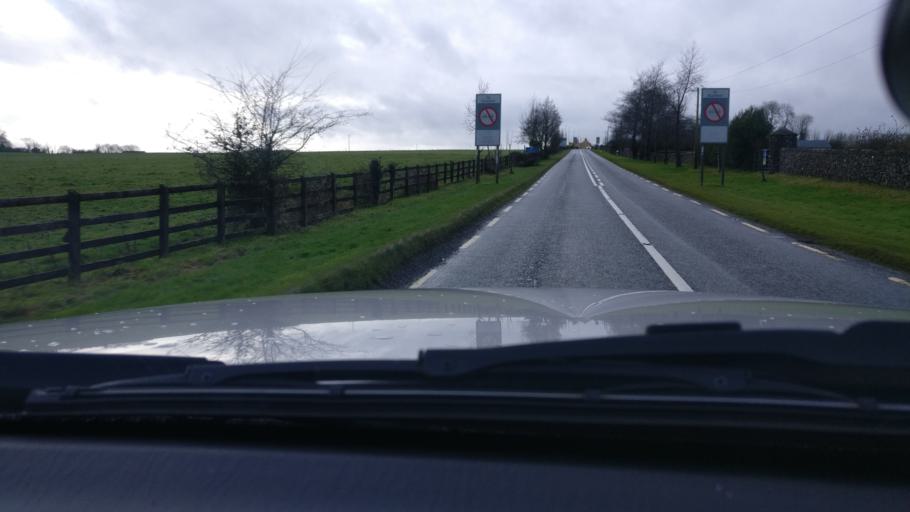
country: IE
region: Leinster
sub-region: An Longfort
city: Edgeworthstown
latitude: 53.6350
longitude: -7.6806
